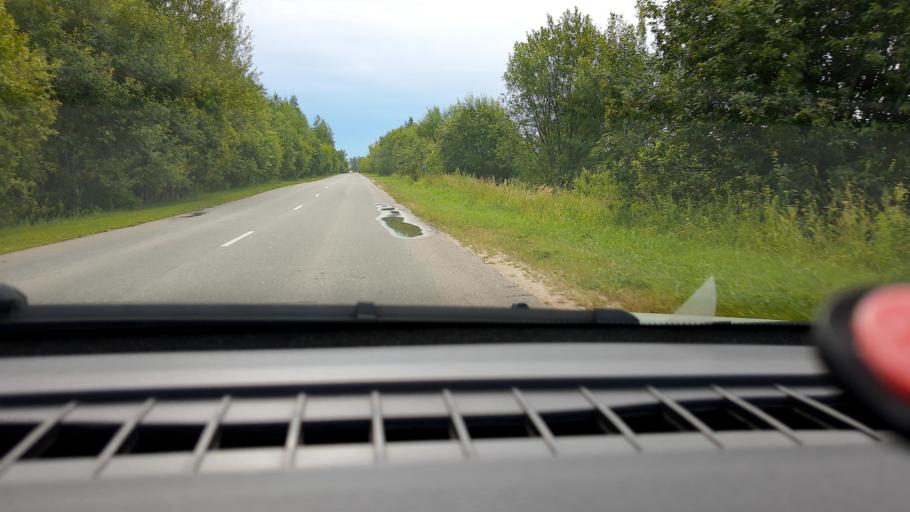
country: RU
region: Nizjnij Novgorod
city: Kstovo
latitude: 56.1502
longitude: 44.2972
